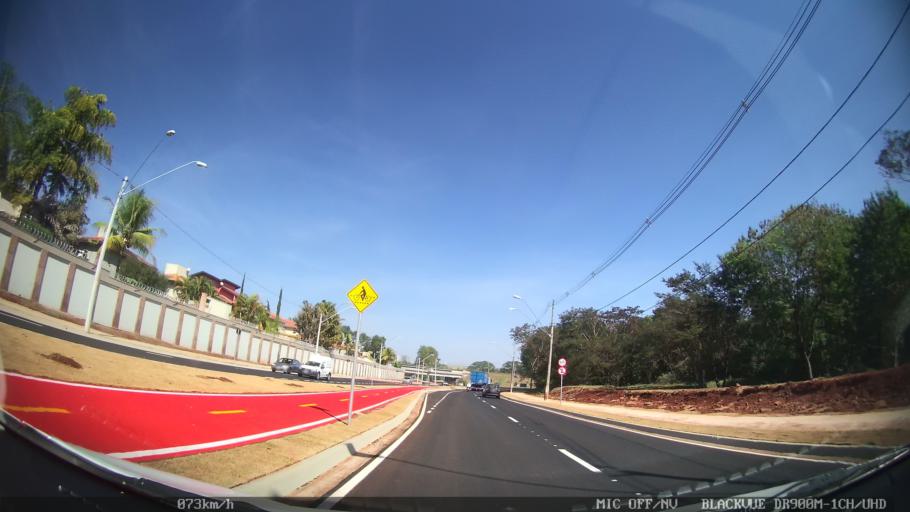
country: BR
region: Sao Paulo
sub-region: Ribeirao Preto
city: Ribeirao Preto
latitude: -21.2138
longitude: -47.8350
